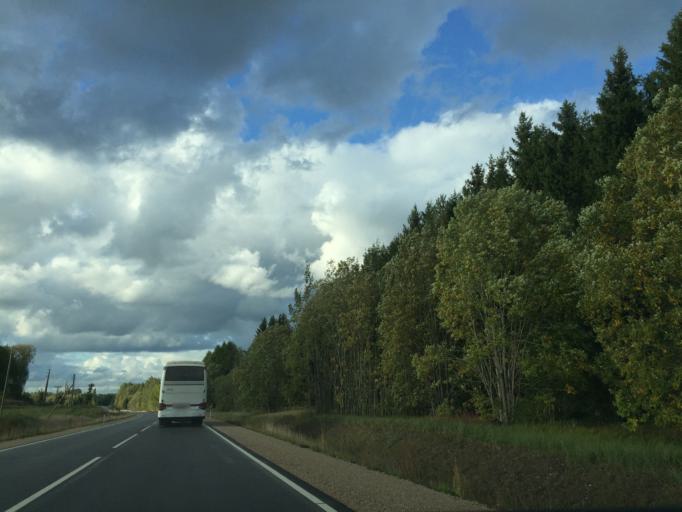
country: LV
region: Ligatne
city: Ligatne
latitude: 57.1427
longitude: 25.0794
